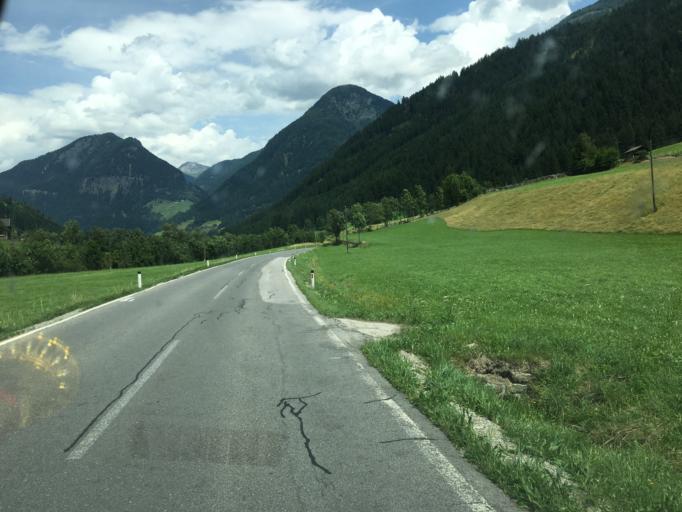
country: AT
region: Carinthia
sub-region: Politischer Bezirk Spittal an der Drau
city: Winklern
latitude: 46.8920
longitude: 12.8976
